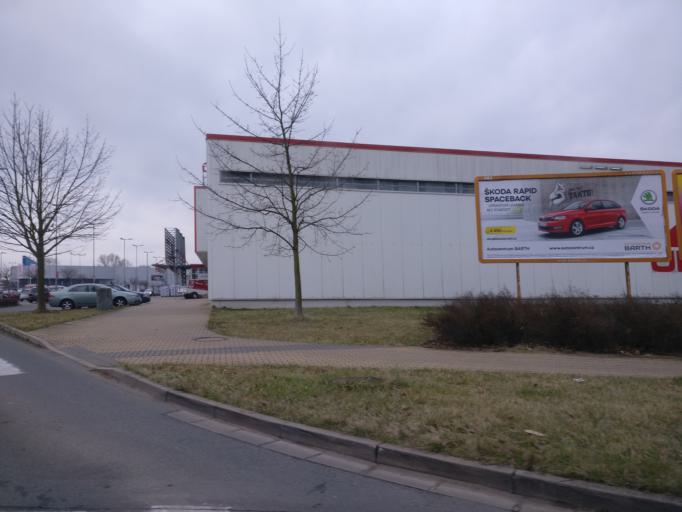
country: CZ
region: Pardubicky
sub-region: Okres Pardubice
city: Pardubice
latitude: 50.0370
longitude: 15.7531
